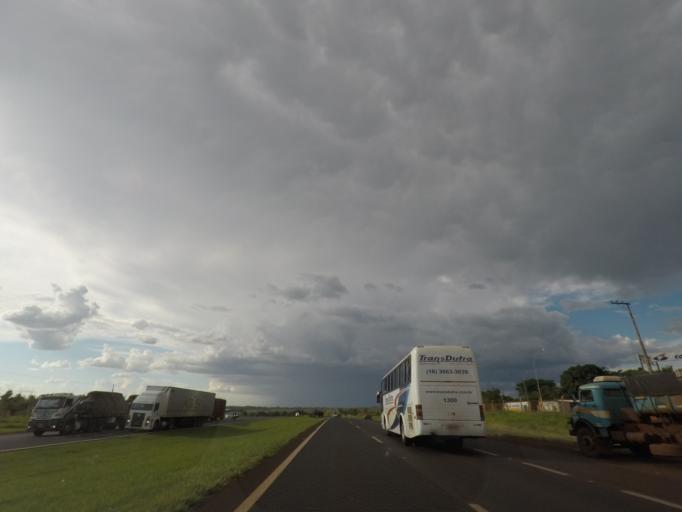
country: BR
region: Sao Paulo
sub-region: Jardinopolis
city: Jardinopolis
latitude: -21.0359
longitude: -47.8324
